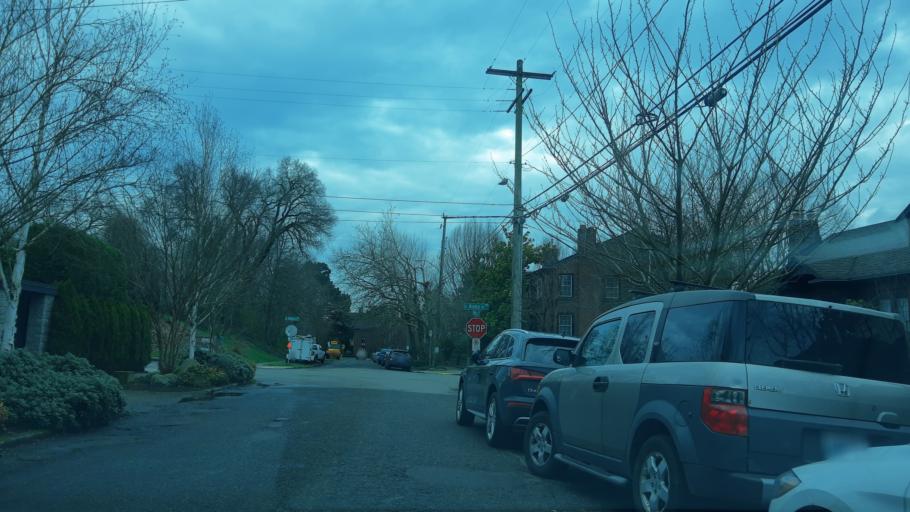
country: US
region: Washington
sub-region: King County
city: Seattle
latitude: 47.6272
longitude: -122.3191
